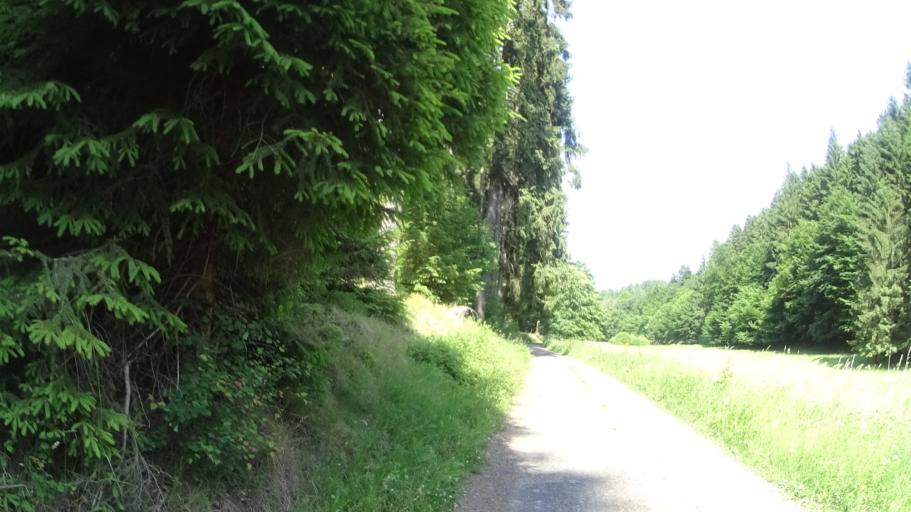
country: DE
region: Hesse
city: Rosenthal
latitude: 50.9672
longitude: 8.8314
